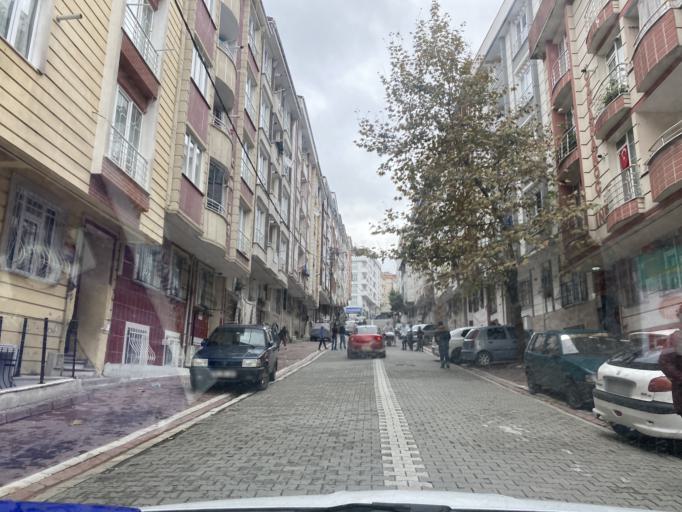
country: TR
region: Istanbul
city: Esenyurt
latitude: 41.0240
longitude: 28.6777
